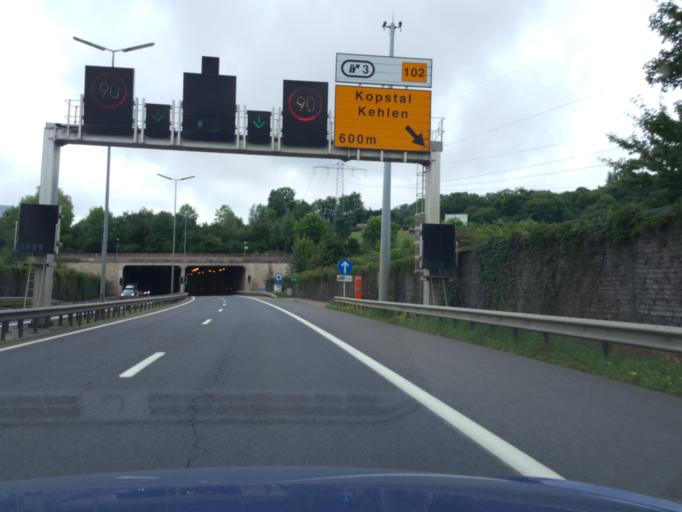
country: LU
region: Luxembourg
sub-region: Canton de Mersch
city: Mersch
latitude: 49.7463
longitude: 6.0901
